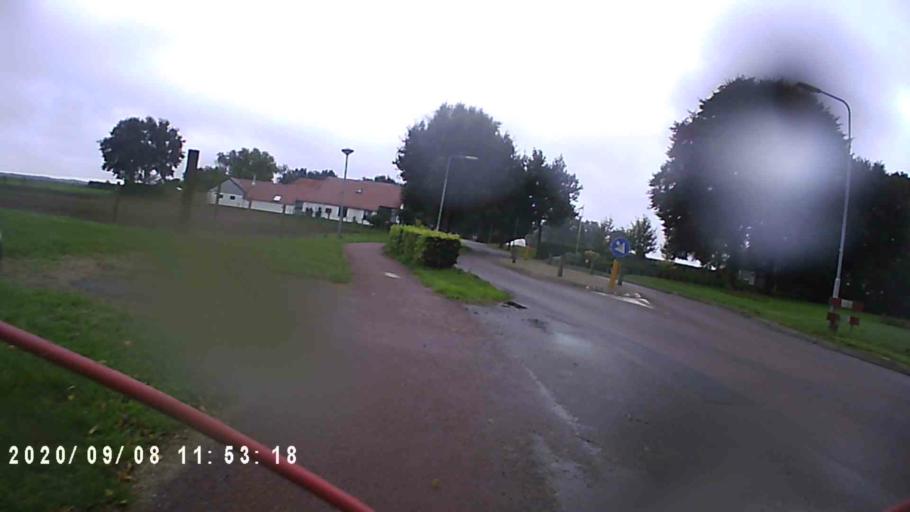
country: NL
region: Groningen
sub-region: Gemeente Hoogezand-Sappemeer
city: Sappemeer
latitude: 53.1215
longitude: 6.8161
